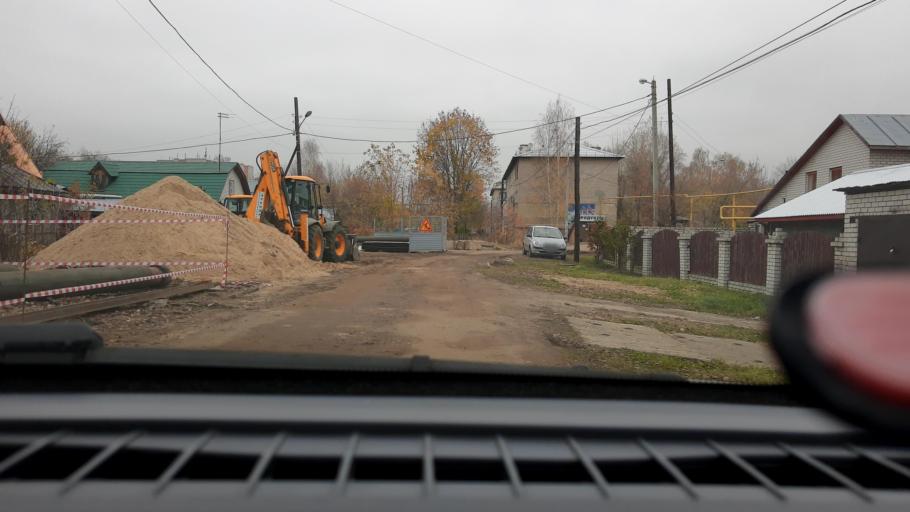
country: RU
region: Nizjnij Novgorod
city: Nizhniy Novgorod
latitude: 56.2771
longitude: 43.9528
